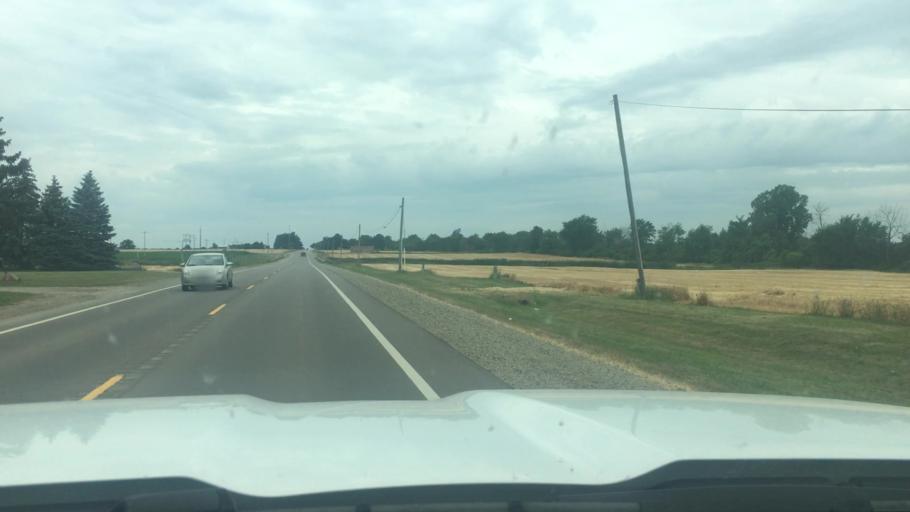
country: US
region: Michigan
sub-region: Clinton County
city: Fowler
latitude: 43.0018
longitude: -84.7530
